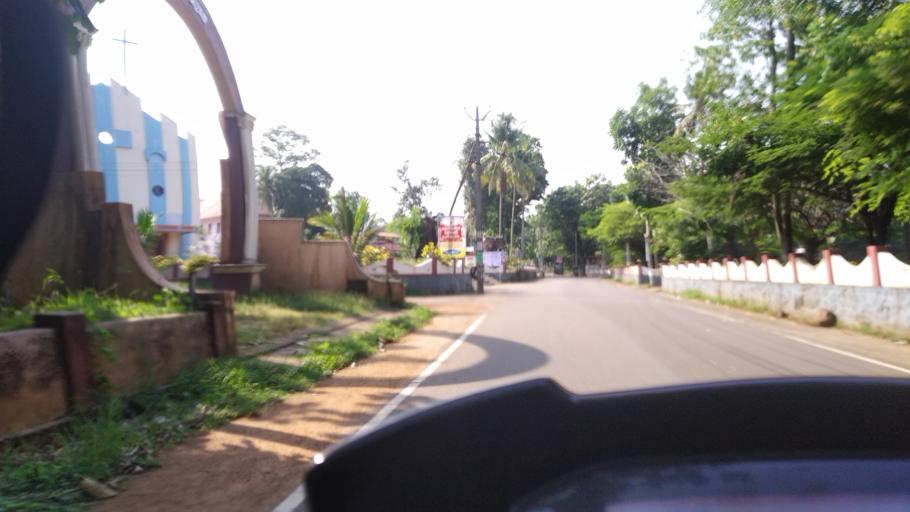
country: IN
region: Kerala
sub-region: Ernakulam
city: Piravam
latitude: 9.8333
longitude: 76.5424
